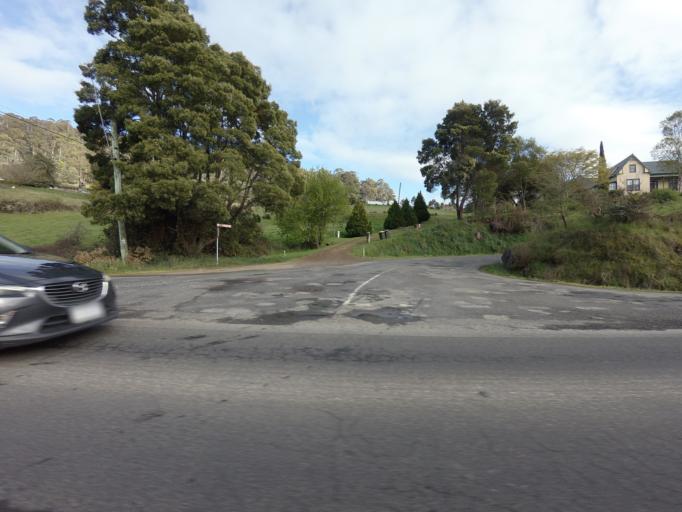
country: AU
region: Tasmania
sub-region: Huon Valley
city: Franklin
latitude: -43.0743
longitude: 147.0165
